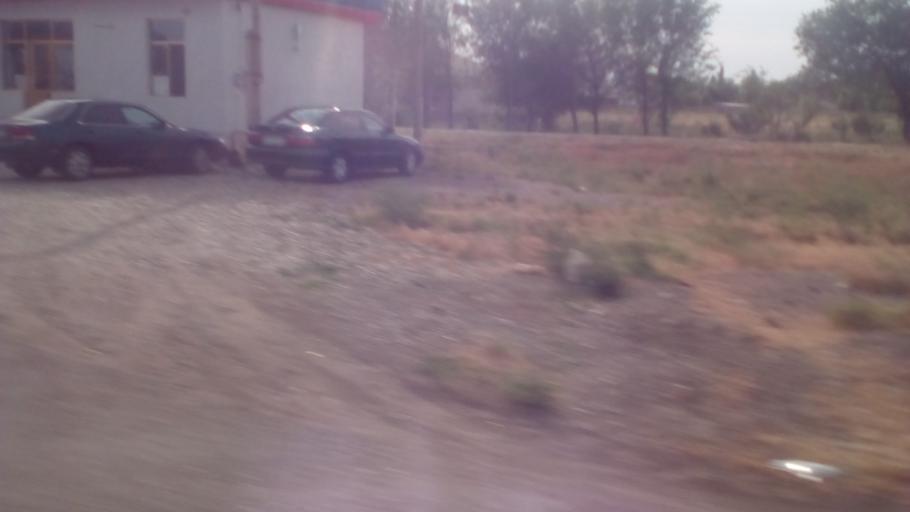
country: KZ
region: Ongtustik Qazaqstan
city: Shayan
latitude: 43.0450
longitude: 69.3895
